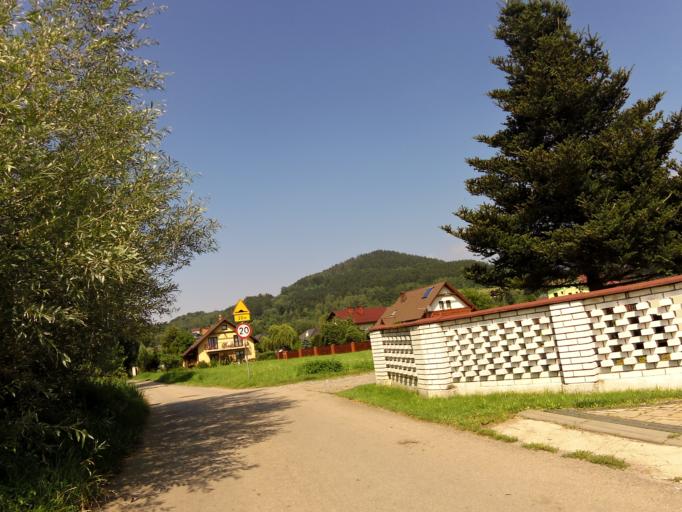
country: PL
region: Silesian Voivodeship
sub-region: Powiat zywiecki
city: Wieprz
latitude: 49.6502
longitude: 19.1790
